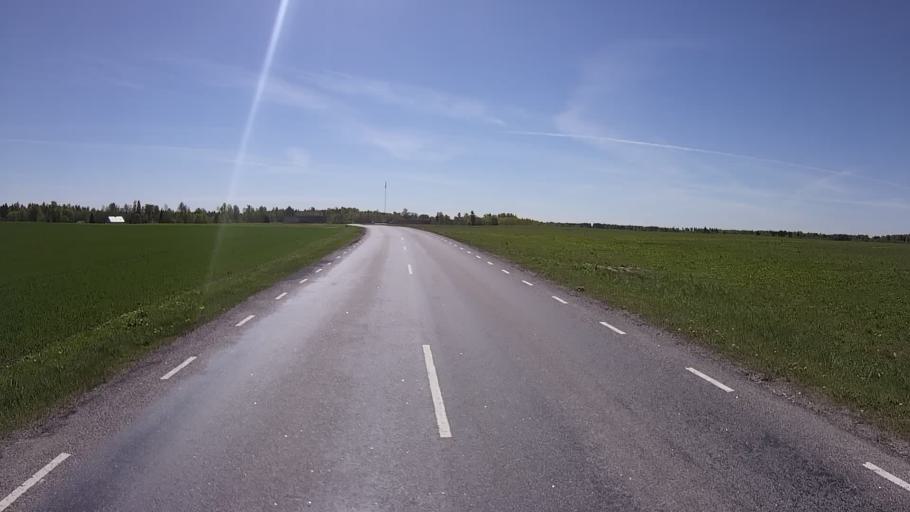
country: EE
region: Harju
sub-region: Raasiku vald
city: Raasiku
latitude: 59.0770
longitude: 25.1648
